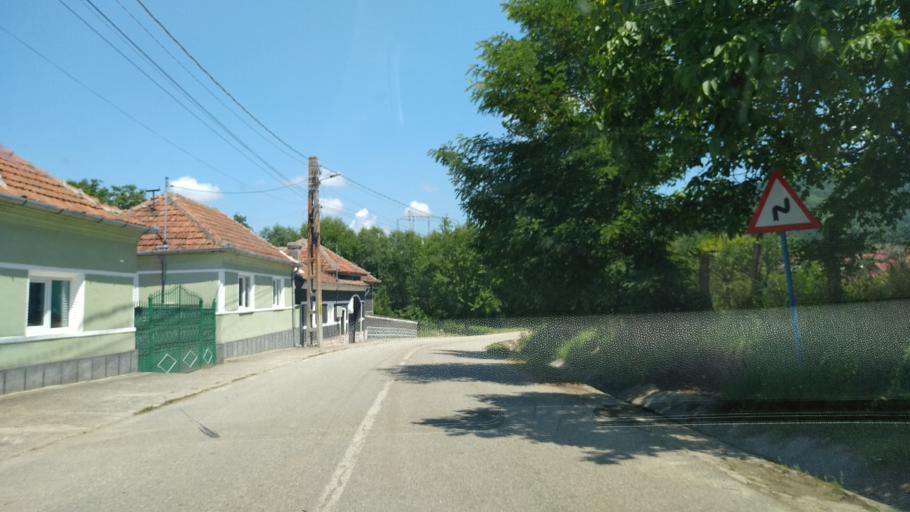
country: RO
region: Hunedoara
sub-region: Comuna Santamaria-Orlea
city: Santamaria-Orlea
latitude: 45.5999
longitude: 23.0116
